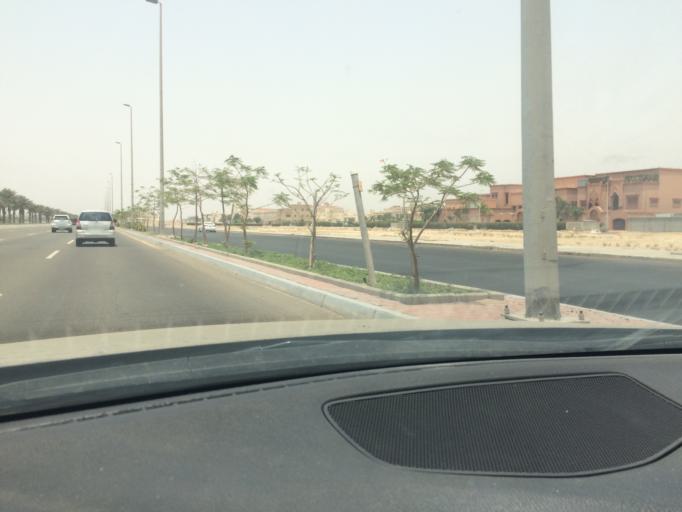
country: SA
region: Makkah
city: Jeddah
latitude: 21.6510
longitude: 39.1115
